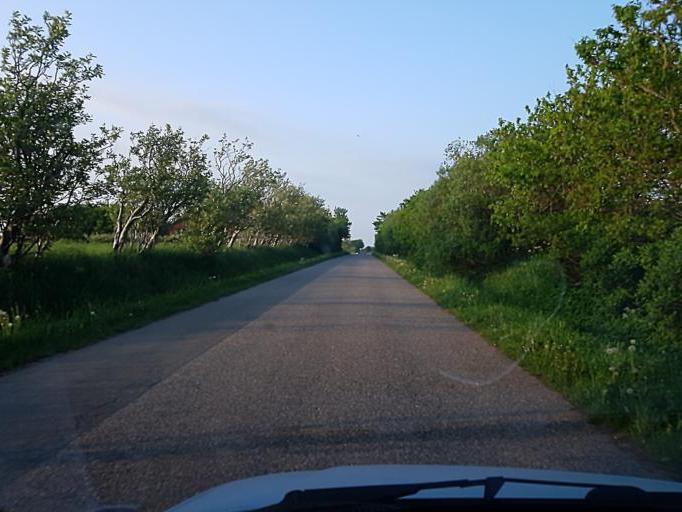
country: DK
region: South Denmark
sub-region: Esbjerg Kommune
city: Tjaereborg
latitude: 55.5518
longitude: 8.5458
